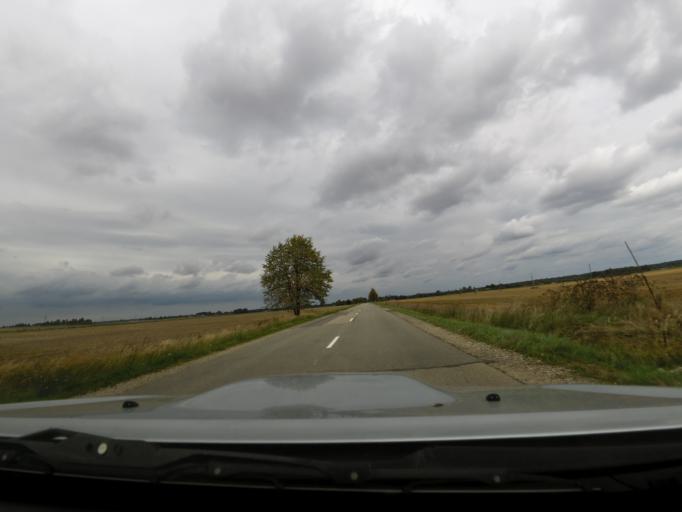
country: LT
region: Panevezys
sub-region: Birzai
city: Birzai
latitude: 56.3023
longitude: 24.8132
